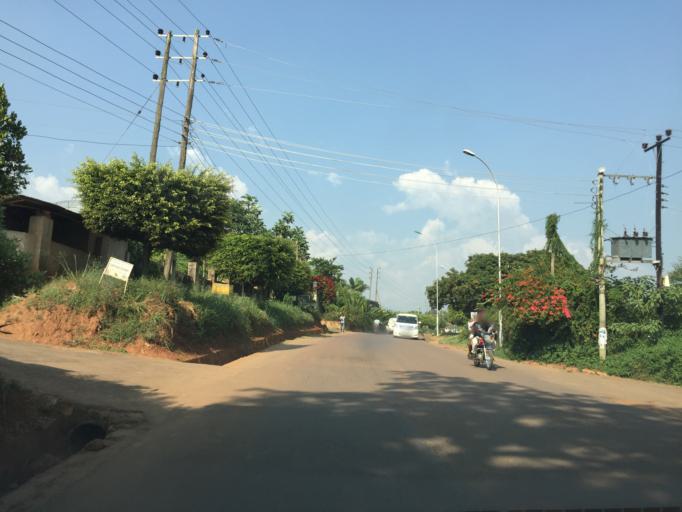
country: UG
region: Central Region
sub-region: Kampala District
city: Kampala
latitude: 0.2413
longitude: 32.6260
